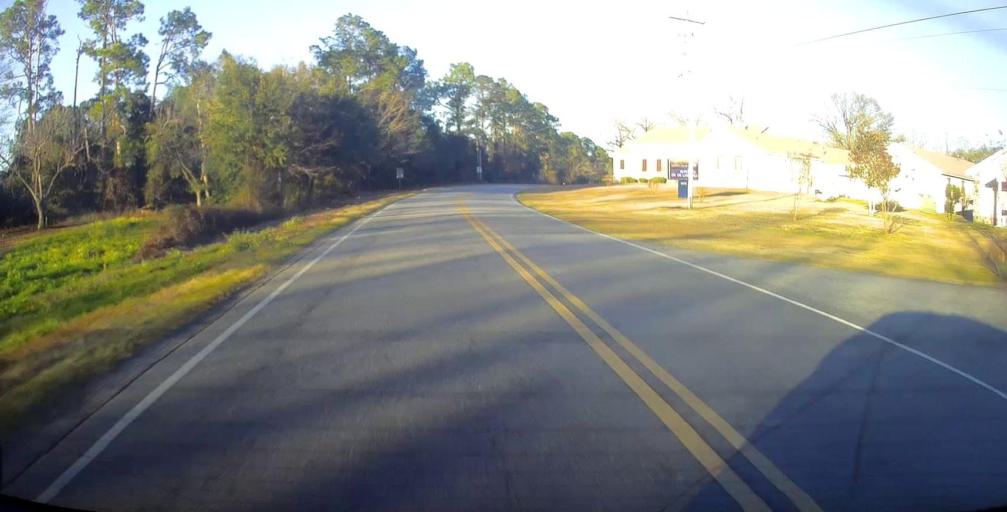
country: US
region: Georgia
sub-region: Dougherty County
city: Albany
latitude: 31.5221
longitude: -84.2286
